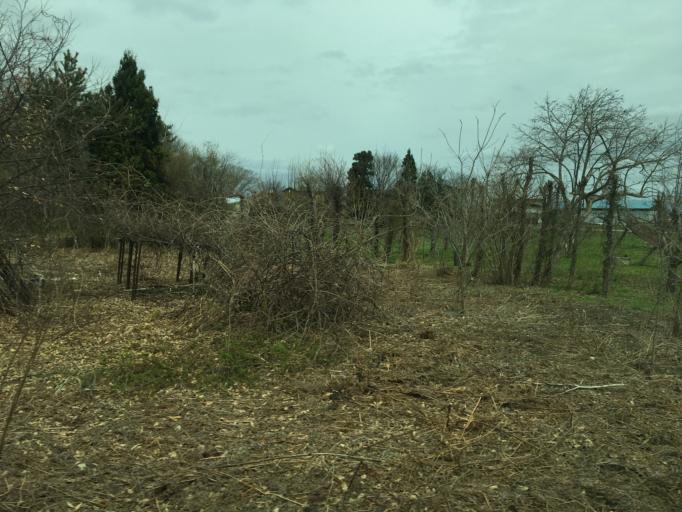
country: JP
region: Aomori
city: Shimokizukuri
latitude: 40.7831
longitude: 140.3244
